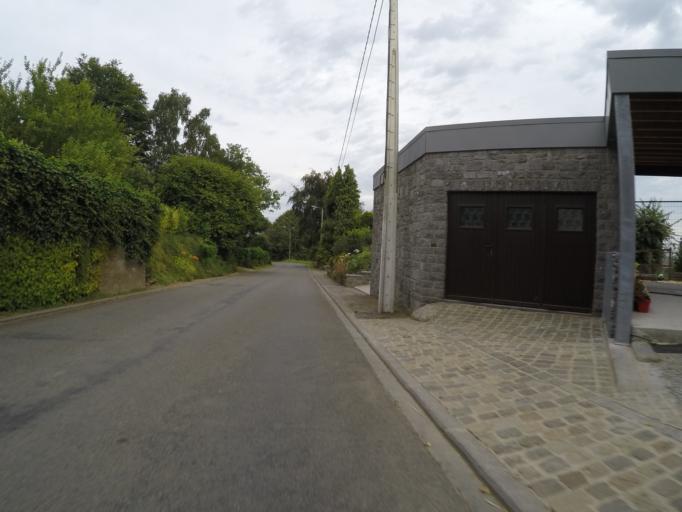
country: BE
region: Wallonia
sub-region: Province de Namur
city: Assesse
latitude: 50.3376
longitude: 4.9814
